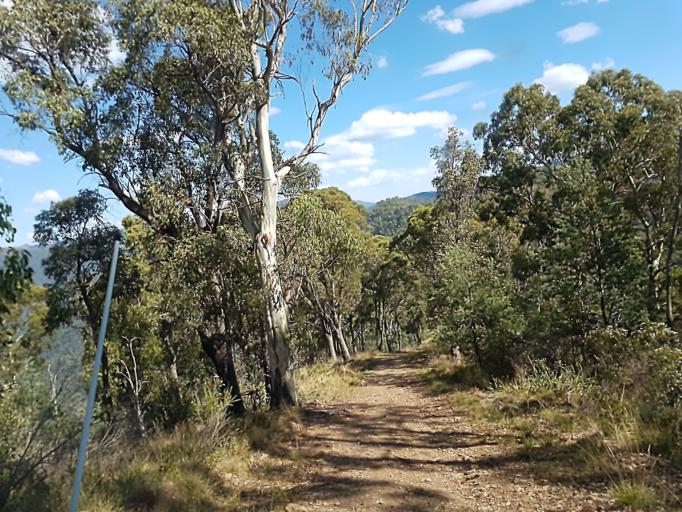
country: AU
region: Victoria
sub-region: Alpine
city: Mount Beauty
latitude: -36.8932
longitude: 147.0266
